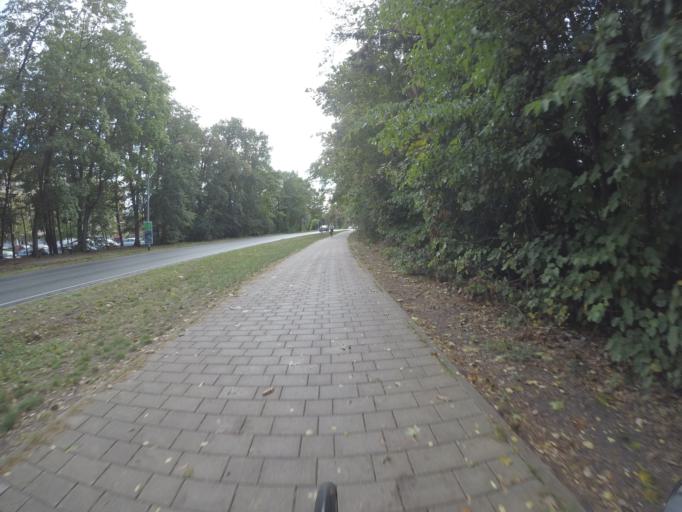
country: DE
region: Brandenburg
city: Strausberg
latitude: 52.5477
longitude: 13.8614
